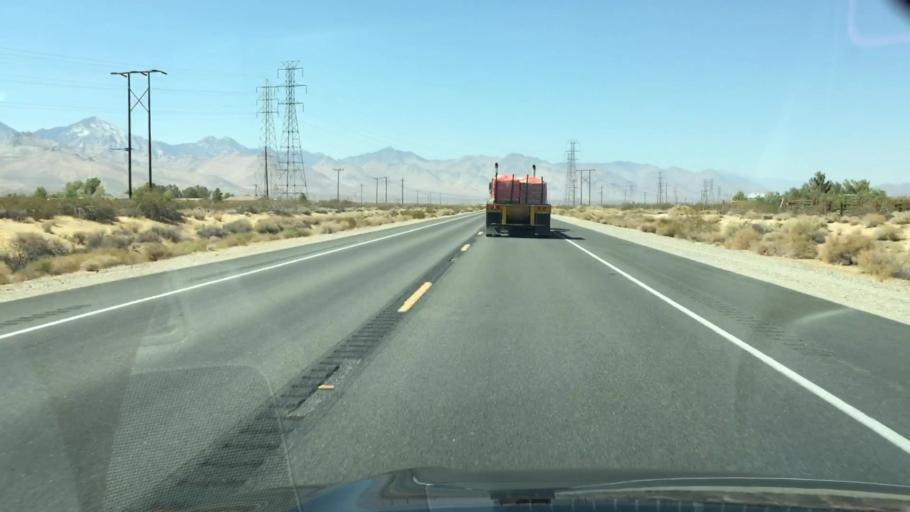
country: US
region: California
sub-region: Kern County
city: Inyokern
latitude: 35.6386
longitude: -117.7895
